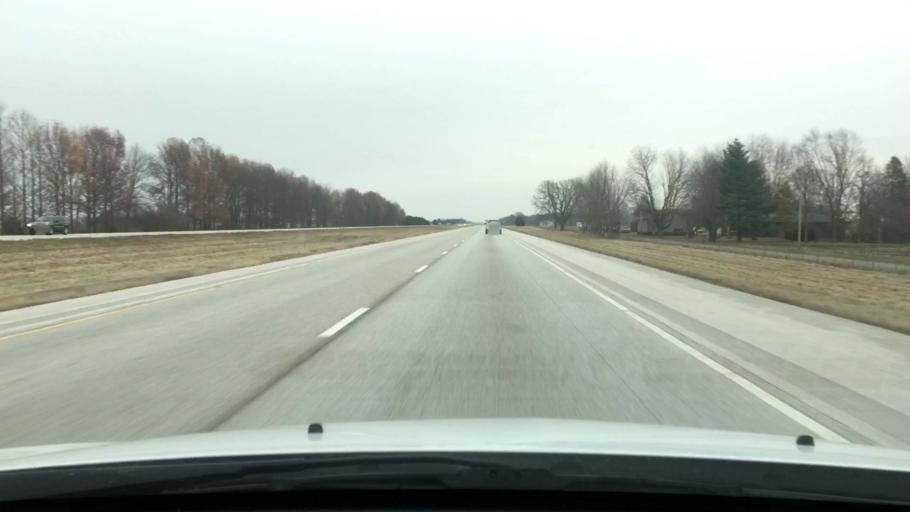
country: US
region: Illinois
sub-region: Morgan County
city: South Jacksonville
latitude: 39.6802
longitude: -90.3229
